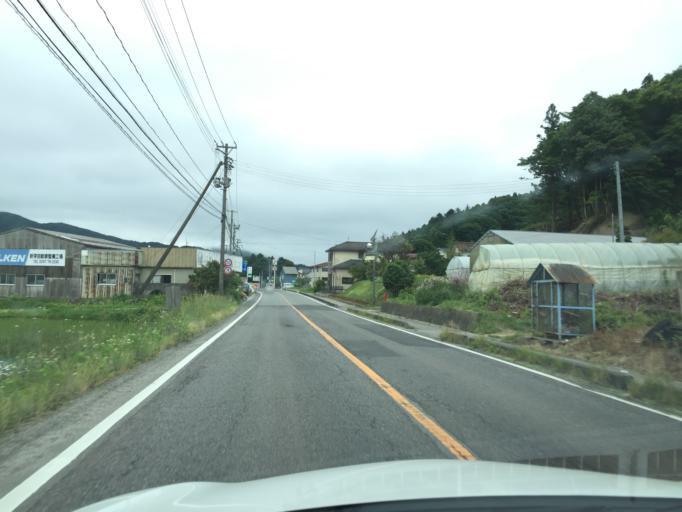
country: JP
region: Fukushima
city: Funehikimachi-funehiki
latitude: 37.3345
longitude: 140.6551
